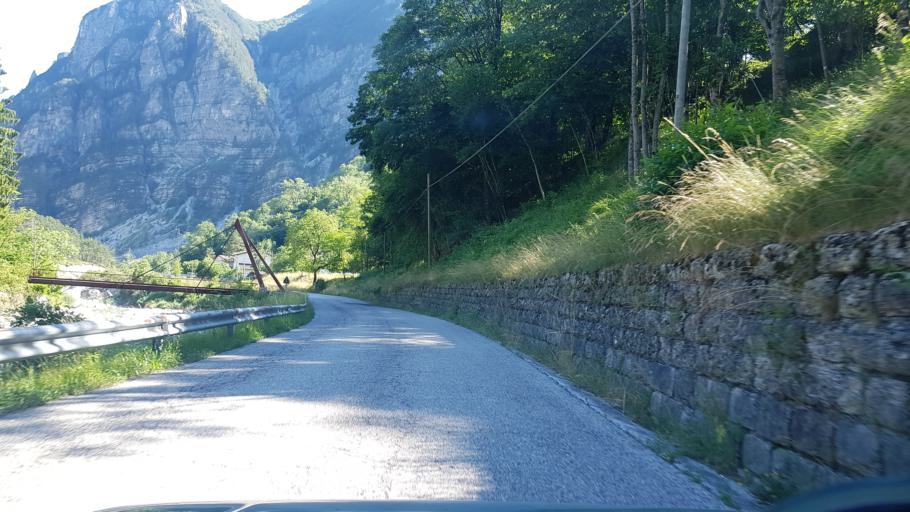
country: IT
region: Friuli Venezia Giulia
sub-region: Provincia di Udine
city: Moggio Udinese
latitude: 46.4525
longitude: 13.1875
